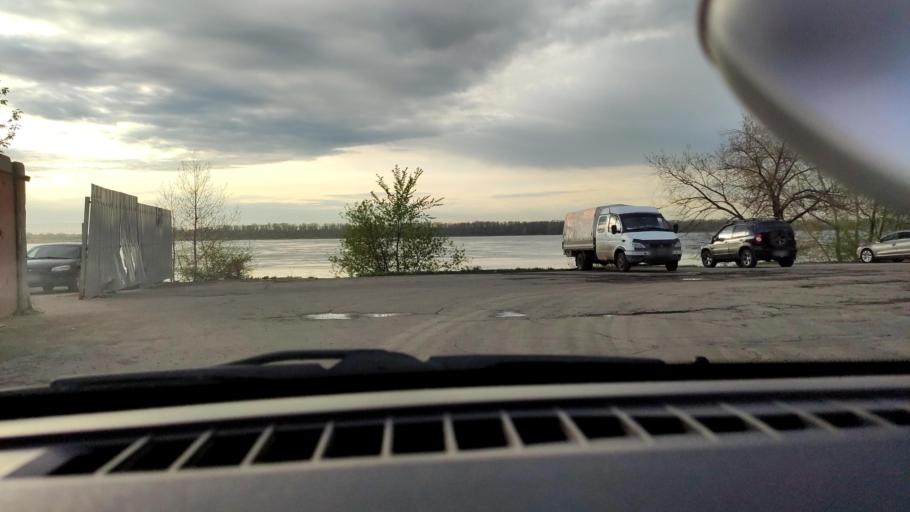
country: RU
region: Samara
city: Rozhdestveno
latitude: 53.1754
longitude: 50.0687
